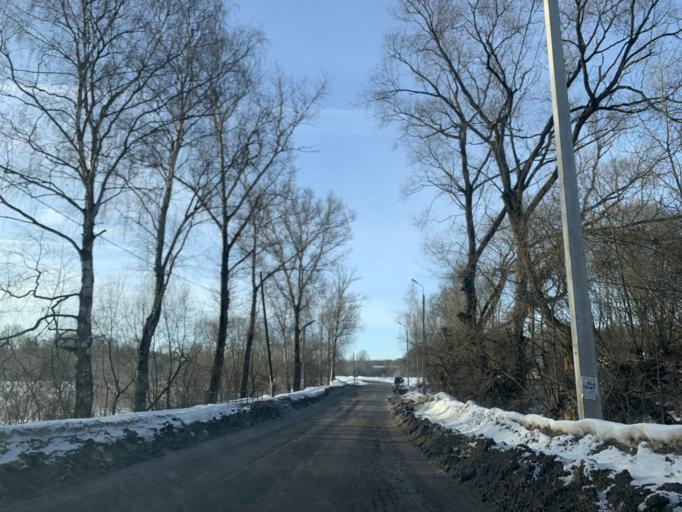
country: RU
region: Jaroslavl
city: Konstantinovskiy
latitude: 57.8232
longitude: 39.5965
